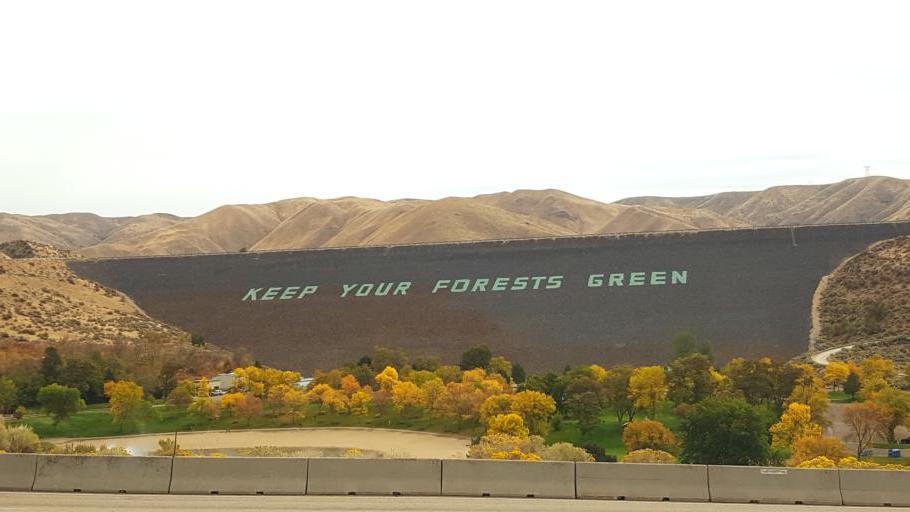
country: US
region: Idaho
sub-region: Ada County
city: Boise
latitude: 43.5339
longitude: -116.1411
